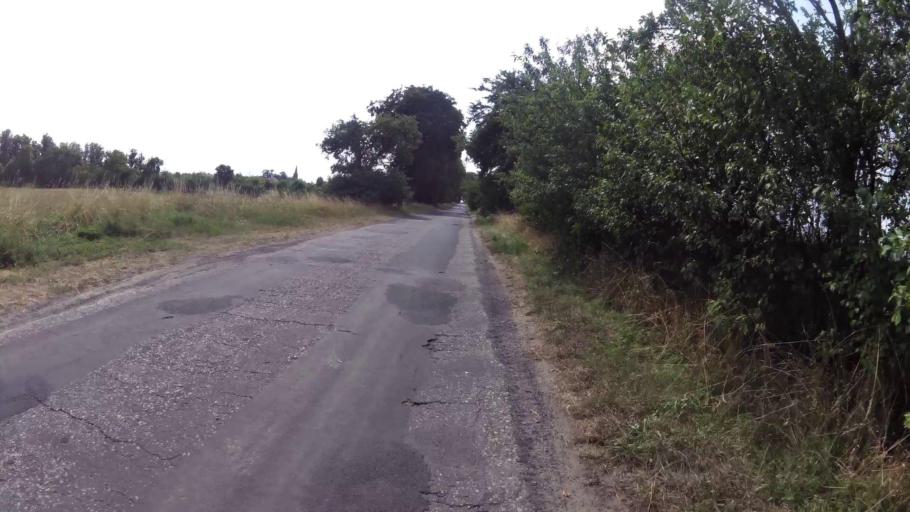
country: PL
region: West Pomeranian Voivodeship
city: Trzcinsko Zdroj
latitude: 52.8948
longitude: 14.5277
